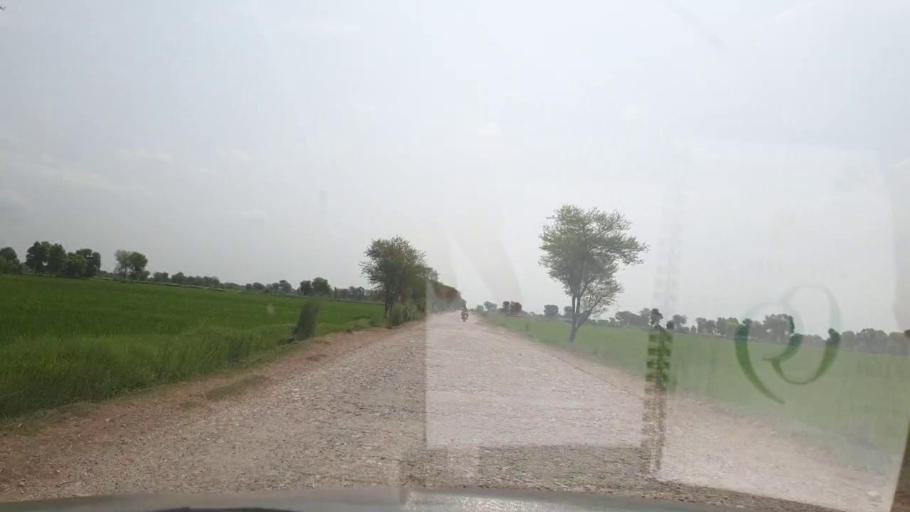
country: PK
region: Sindh
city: Ratodero
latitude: 27.8425
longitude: 68.3150
